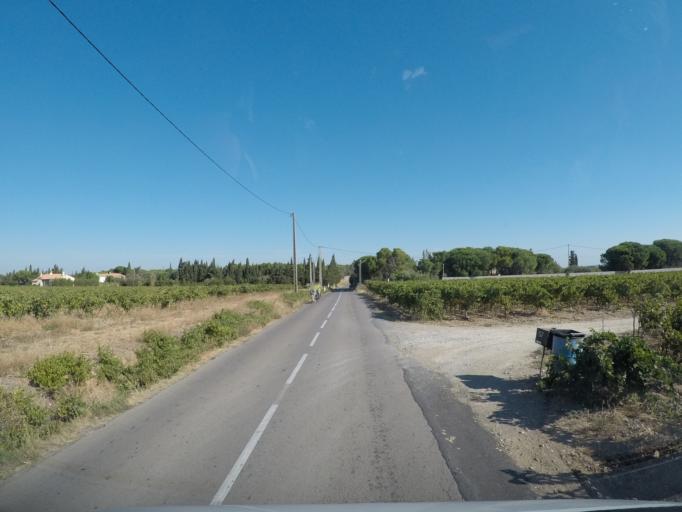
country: FR
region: Languedoc-Roussillon
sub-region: Departement de l'Aude
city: Narbonne
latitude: 43.1526
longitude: 3.0087
